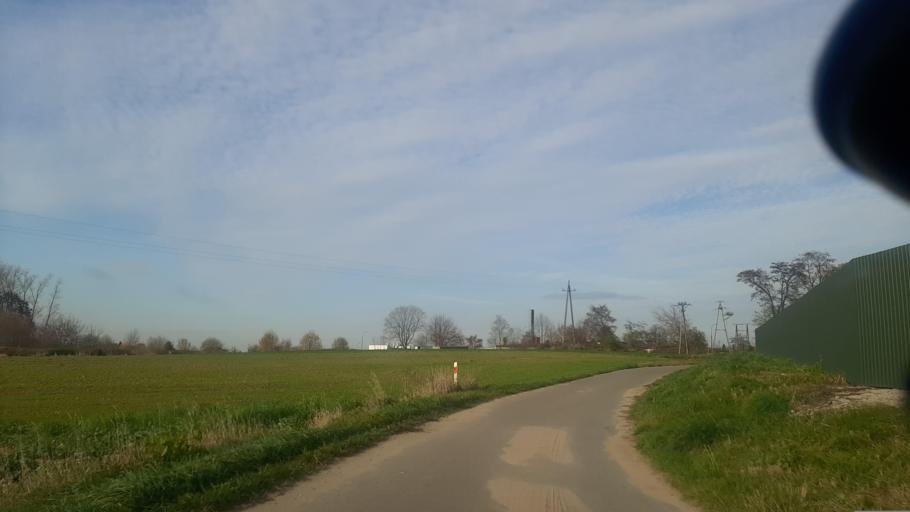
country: PL
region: Lublin Voivodeship
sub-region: Powiat pulawski
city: Markuszow
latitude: 51.3697
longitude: 22.2708
